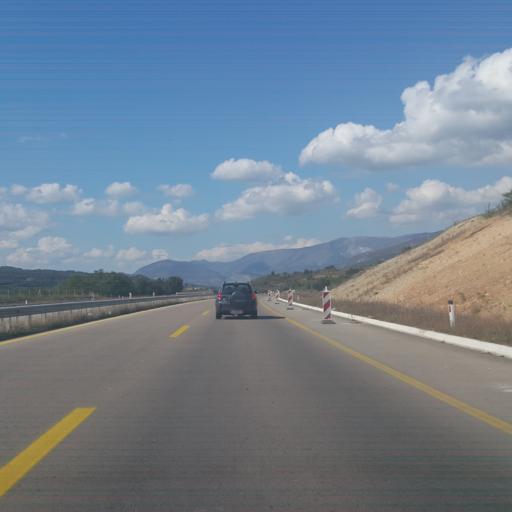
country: RS
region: Central Serbia
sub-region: Pirotski Okrug
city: Bela Palanka
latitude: 43.2413
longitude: 22.2848
